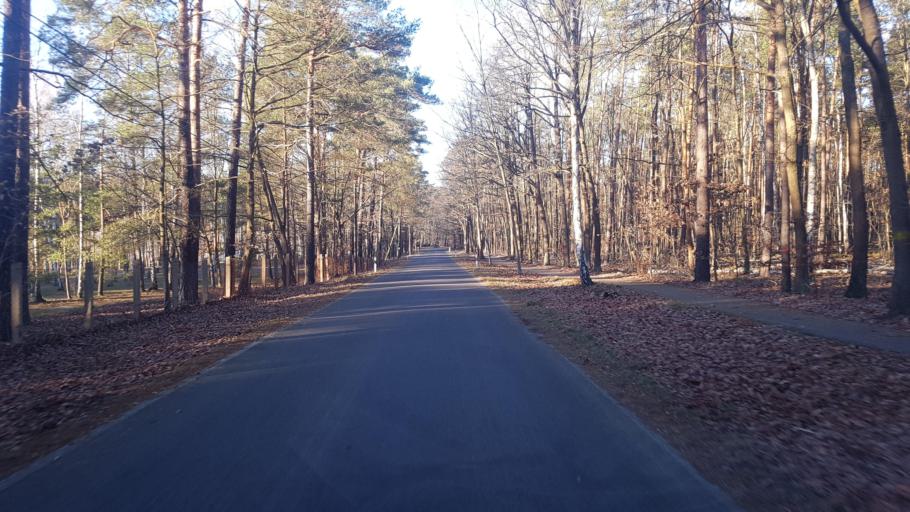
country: DE
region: Brandenburg
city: Tauer
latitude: 51.9338
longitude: 14.4803
